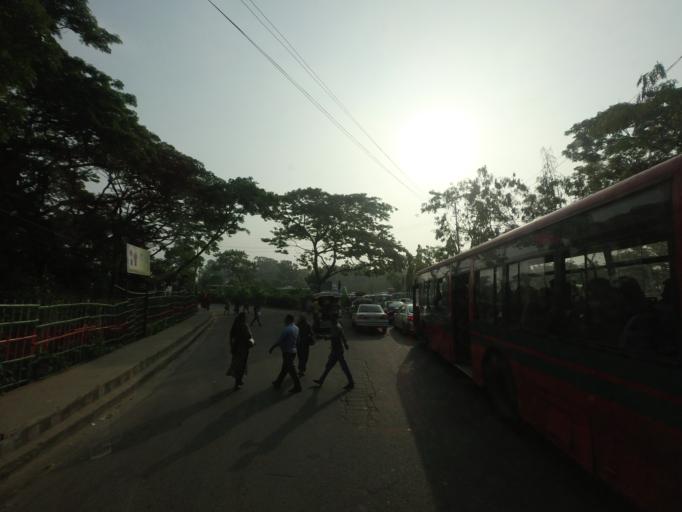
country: BD
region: Dhaka
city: Azimpur
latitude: 23.7767
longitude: 90.3800
